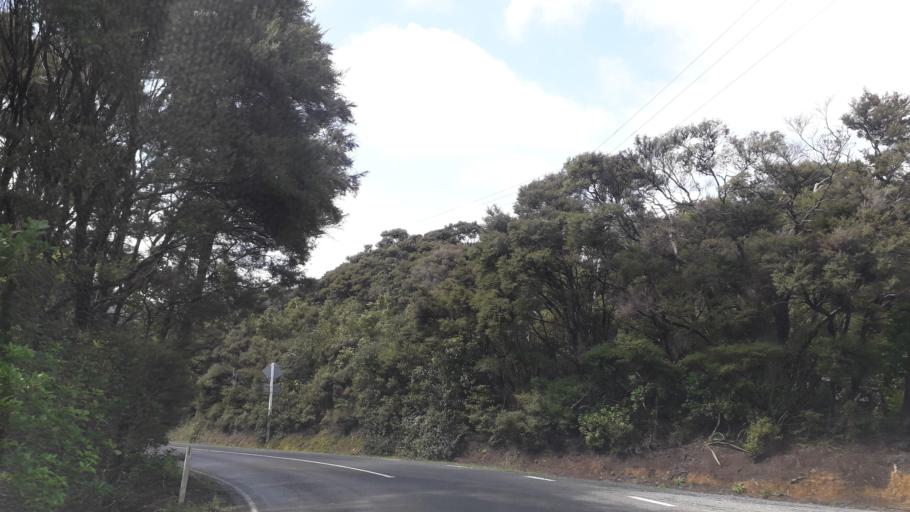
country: NZ
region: Northland
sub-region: Far North District
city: Paihia
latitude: -35.2440
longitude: 174.2485
